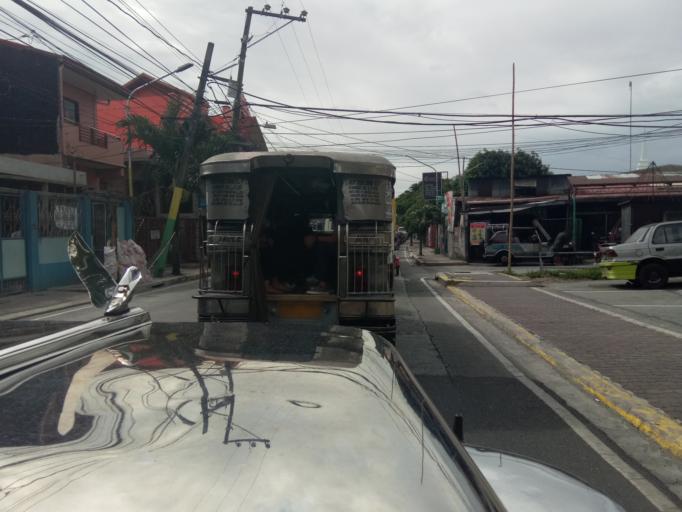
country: PH
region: Calabarzon
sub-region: Province of Cavite
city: Dasmarinas
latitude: 14.3182
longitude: 120.9420
